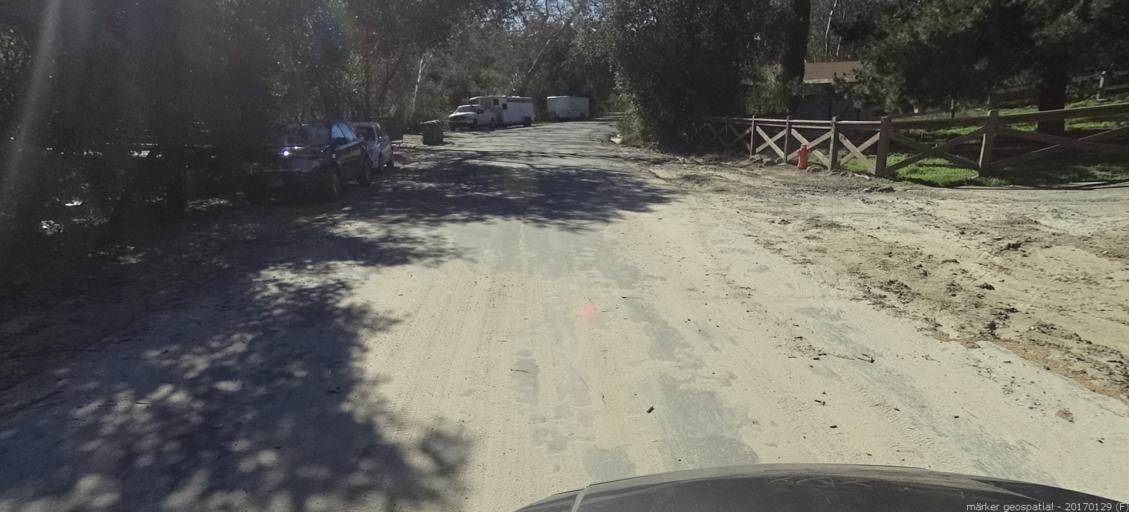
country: US
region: California
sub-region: Orange County
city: Trabuco Canyon
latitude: 33.6712
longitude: -117.5876
